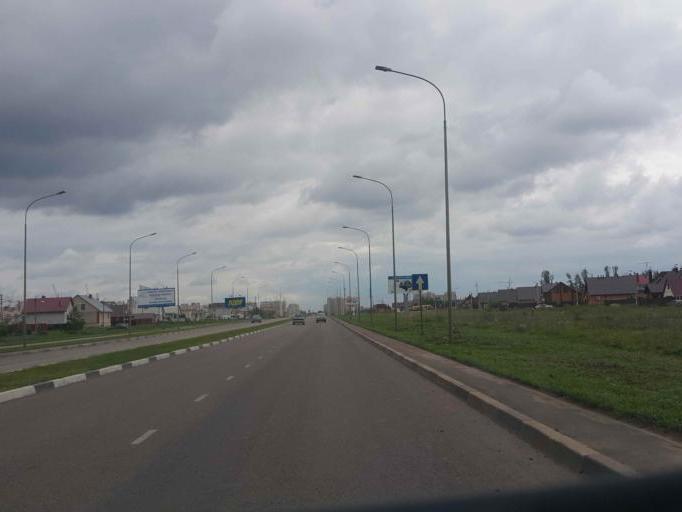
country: RU
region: Tambov
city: Tambov
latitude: 52.7780
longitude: 41.3797
